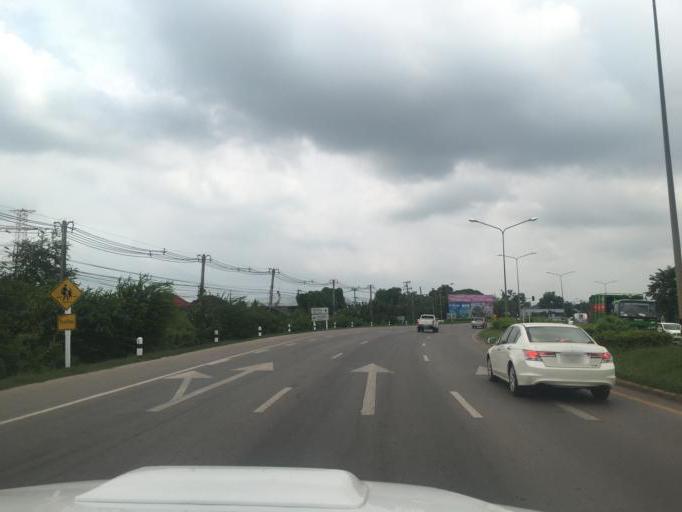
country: TH
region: Changwat Udon Thani
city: Udon Thani
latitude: 17.3900
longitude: 102.7661
